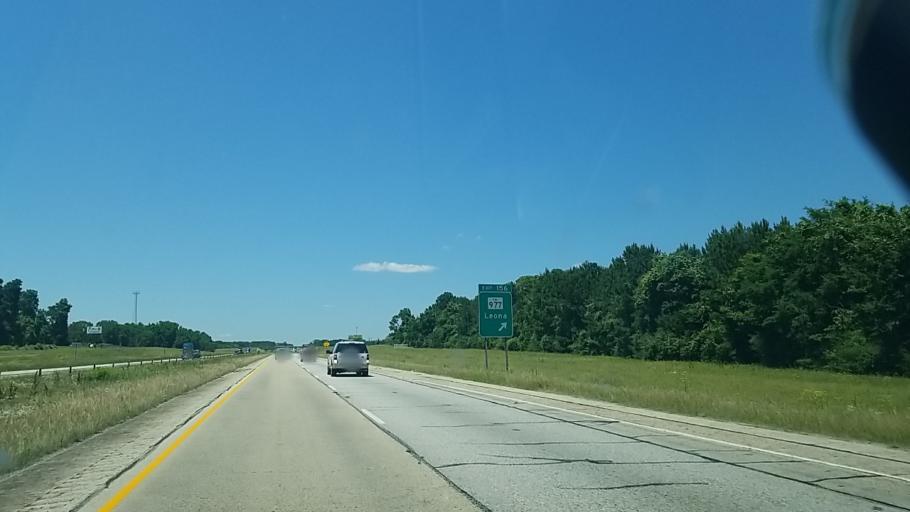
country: US
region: Texas
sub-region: Leon County
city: Centerville
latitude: 31.1412
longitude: -95.9808
